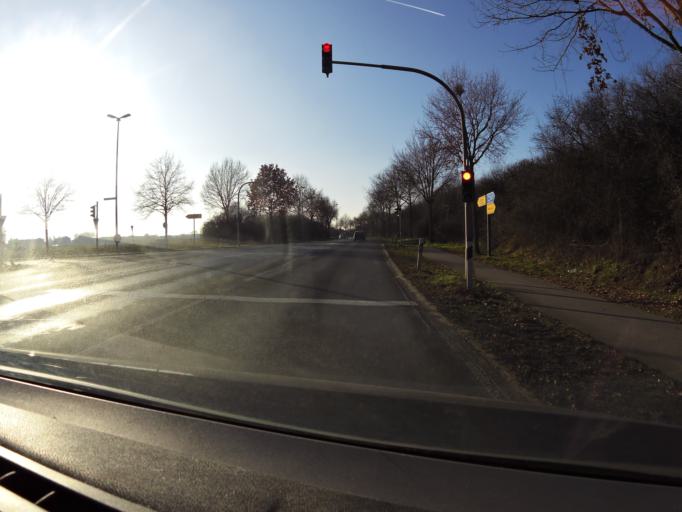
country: DE
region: North Rhine-Westphalia
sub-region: Regierungsbezirk Dusseldorf
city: Bruggen
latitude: 51.2929
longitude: 6.1961
